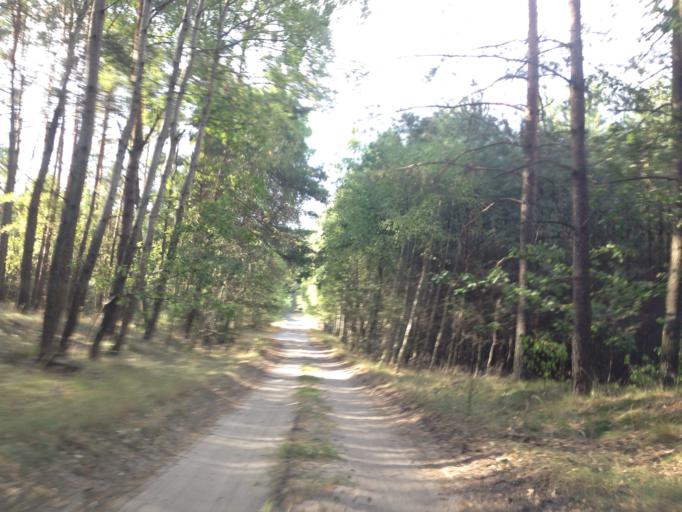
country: PL
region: Kujawsko-Pomorskie
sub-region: Powiat swiecki
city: Swiekatowo
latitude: 53.4958
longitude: 18.1223
